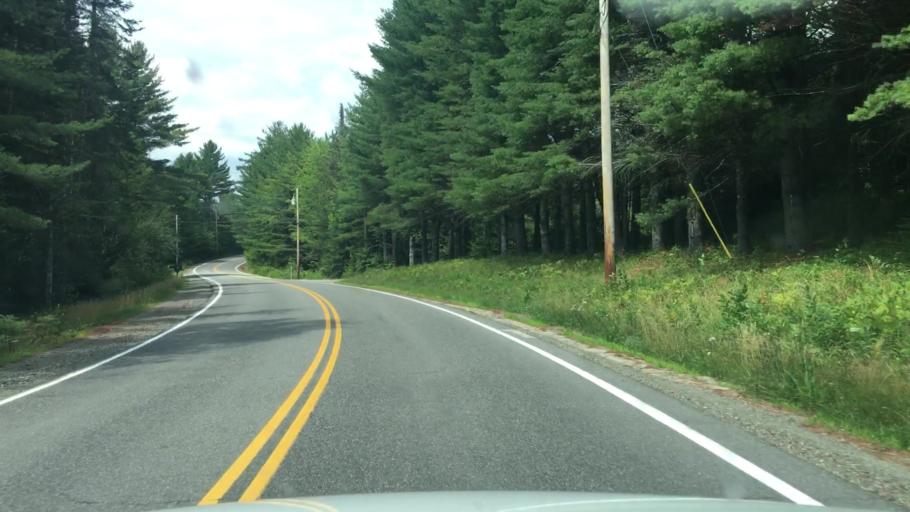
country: US
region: New Hampshire
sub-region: Coos County
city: Whitefield
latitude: 44.3057
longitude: -71.6582
